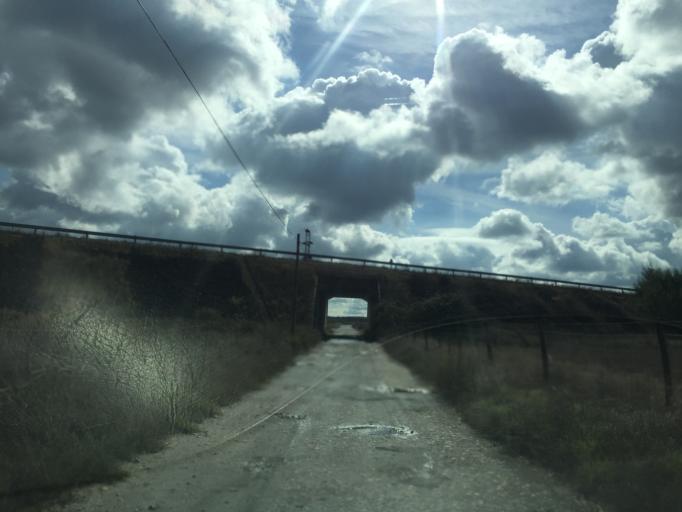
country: PT
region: Santarem
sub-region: Coruche
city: Coruche
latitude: 38.9393
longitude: -8.5156
